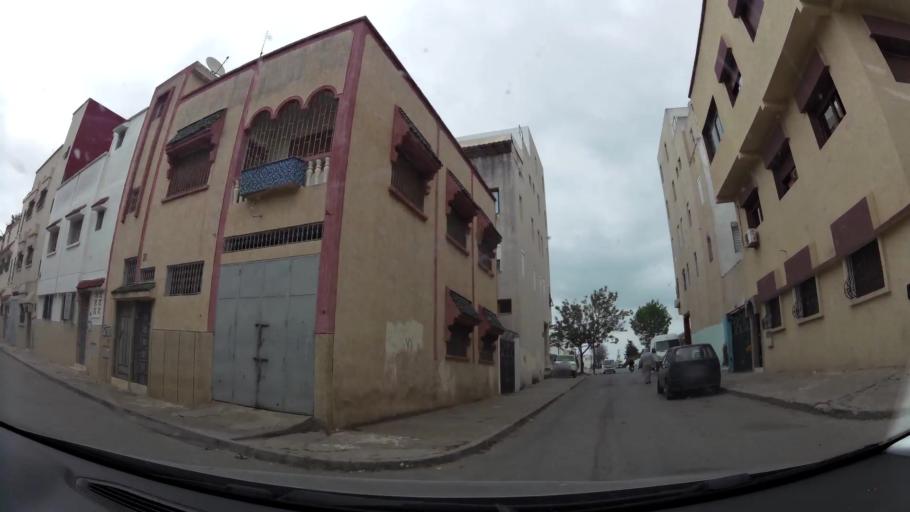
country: MA
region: Rabat-Sale-Zemmour-Zaer
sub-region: Rabat
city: Rabat
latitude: 33.9808
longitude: -6.8130
